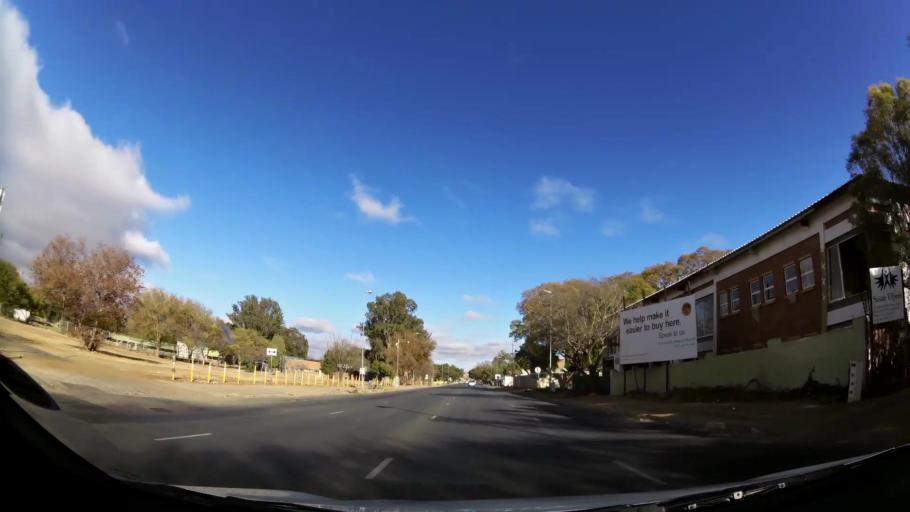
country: ZA
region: Limpopo
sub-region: Capricorn District Municipality
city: Polokwane
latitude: -23.9194
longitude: 29.4592
